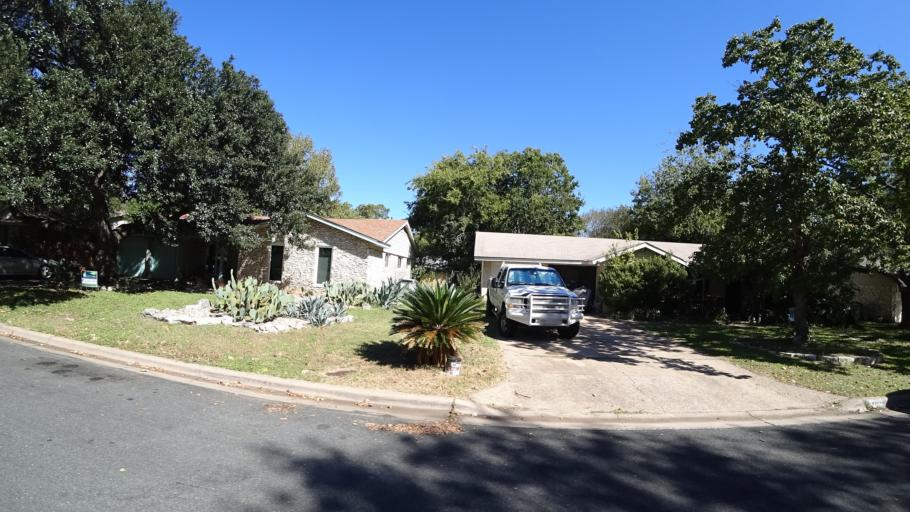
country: US
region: Texas
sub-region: Travis County
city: Rollingwood
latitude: 30.2194
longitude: -97.7988
